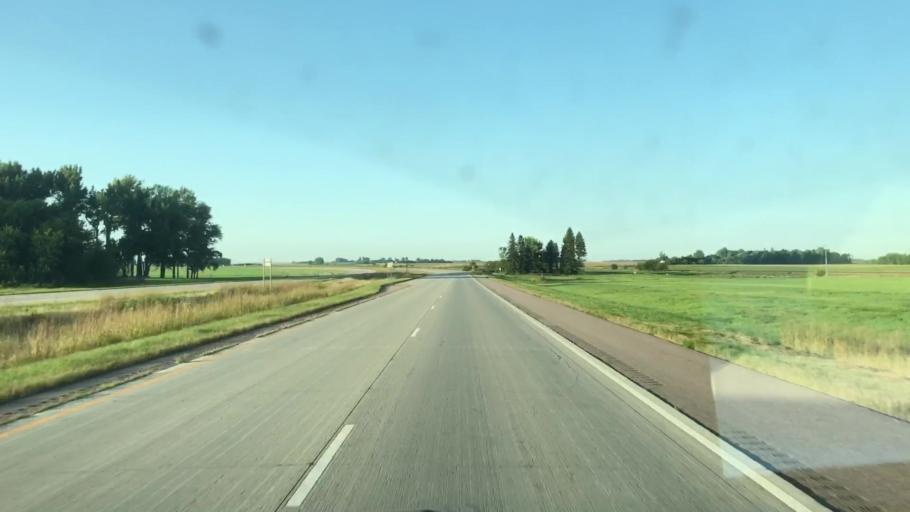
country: US
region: Minnesota
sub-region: Nobles County
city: Worthington
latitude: 43.5798
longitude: -95.6511
